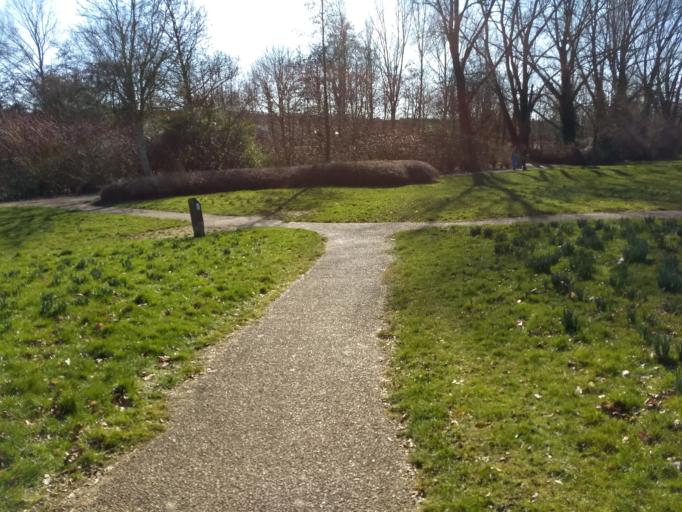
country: GB
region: England
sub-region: Milton Keynes
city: Shenley Church End
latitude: 52.0043
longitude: -0.7712
